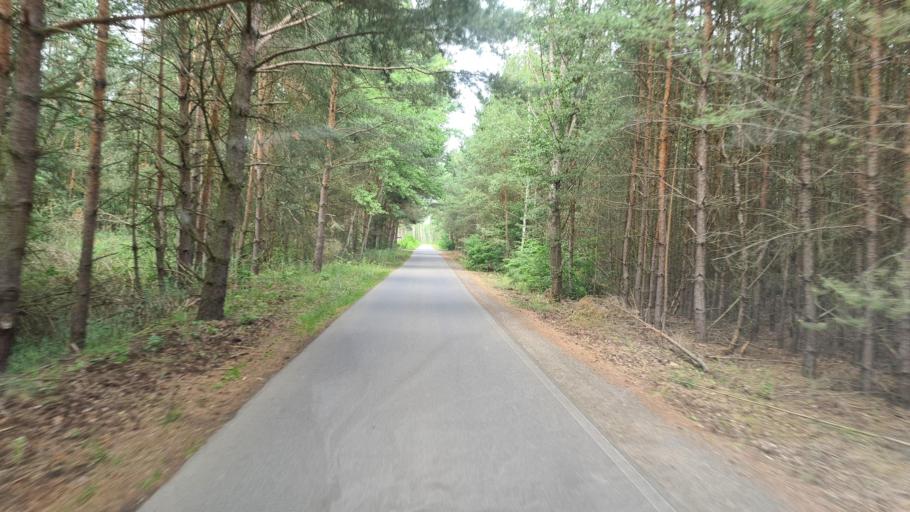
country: DE
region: Brandenburg
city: Neupetershain
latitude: 51.6806
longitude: 14.1167
